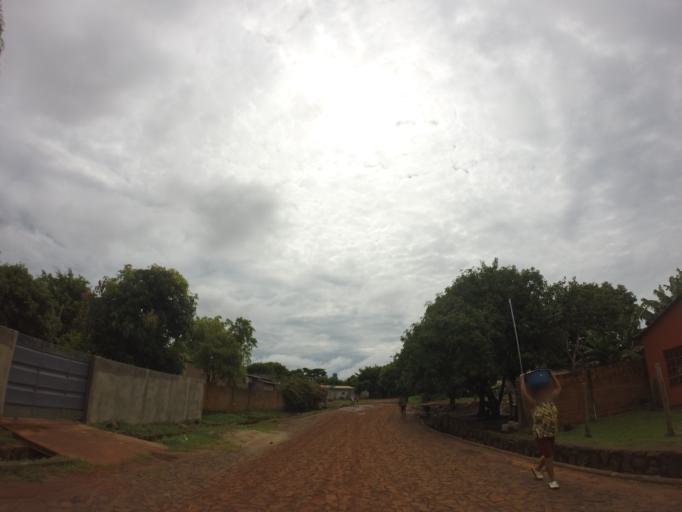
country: PY
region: Alto Parana
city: Ciudad del Este
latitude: -25.3999
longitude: -54.6366
